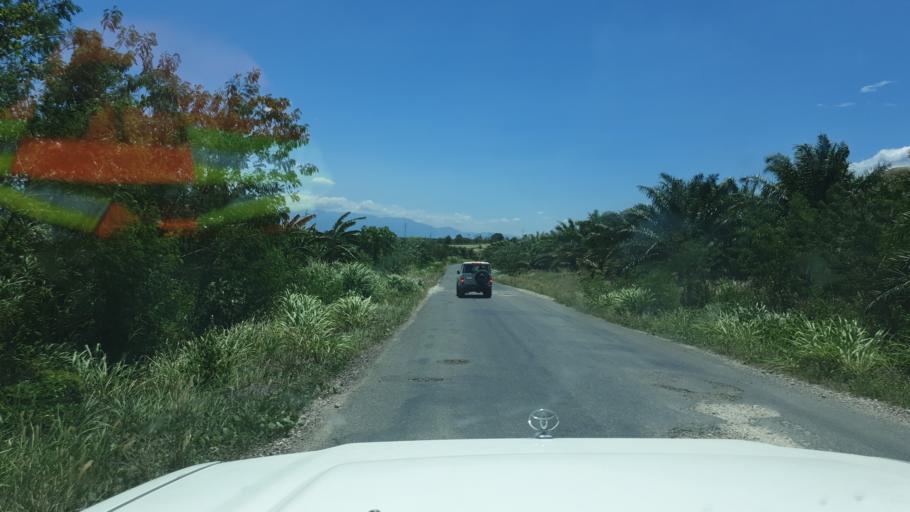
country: PG
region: Eastern Highlands
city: Goroka
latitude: -5.8123
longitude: 145.6417
